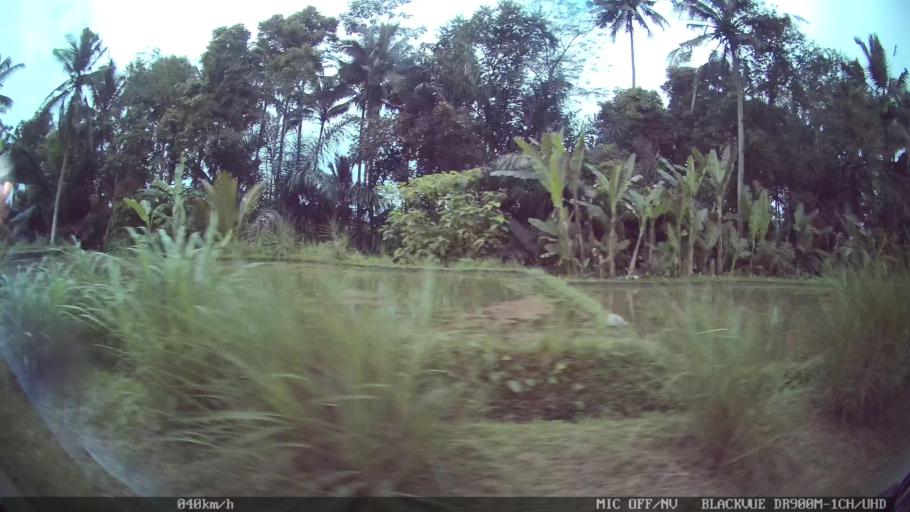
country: ID
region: Bali
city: Bunutan
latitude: -8.4629
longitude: 115.2341
